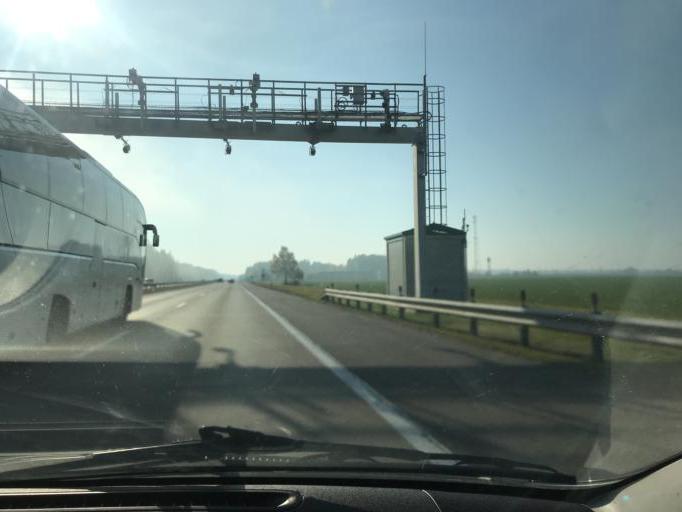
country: BY
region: Minsk
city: Samakhvalavichy
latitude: 53.5681
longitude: 27.4713
